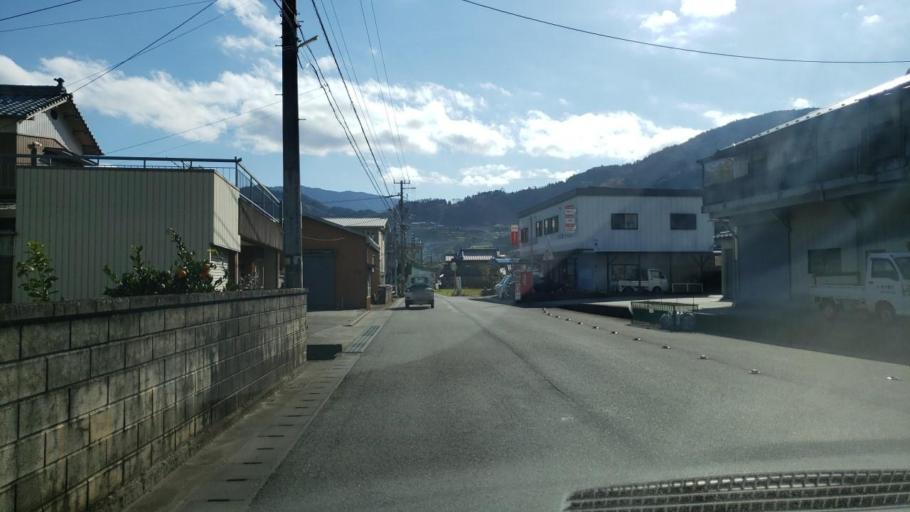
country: JP
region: Tokushima
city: Wakimachi
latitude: 34.0334
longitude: 134.0292
